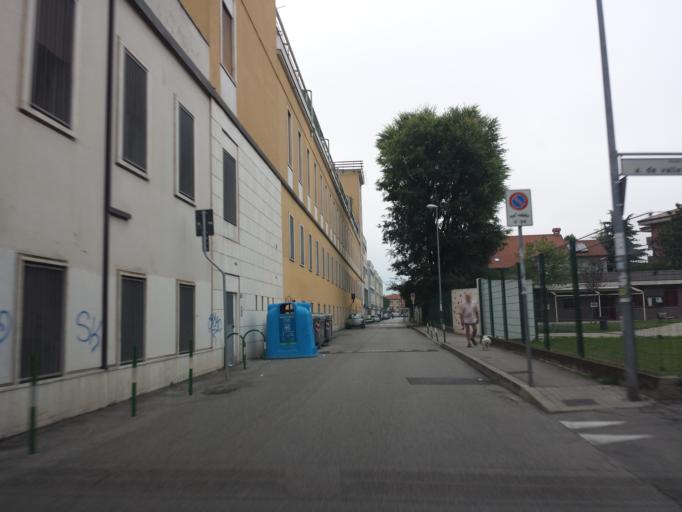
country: IT
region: Veneto
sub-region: Provincia di Padova
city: Padova
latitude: 45.4239
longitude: 11.8792
